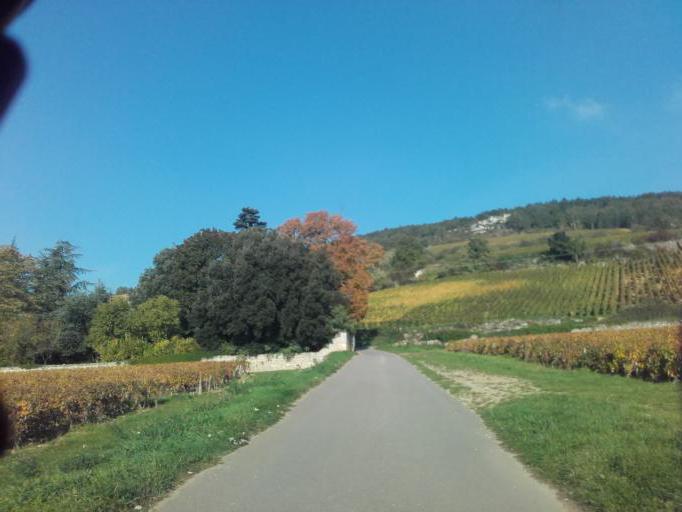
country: FR
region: Bourgogne
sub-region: Departement de Saone-et-Loire
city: Chagny
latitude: 46.9156
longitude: 4.6977
